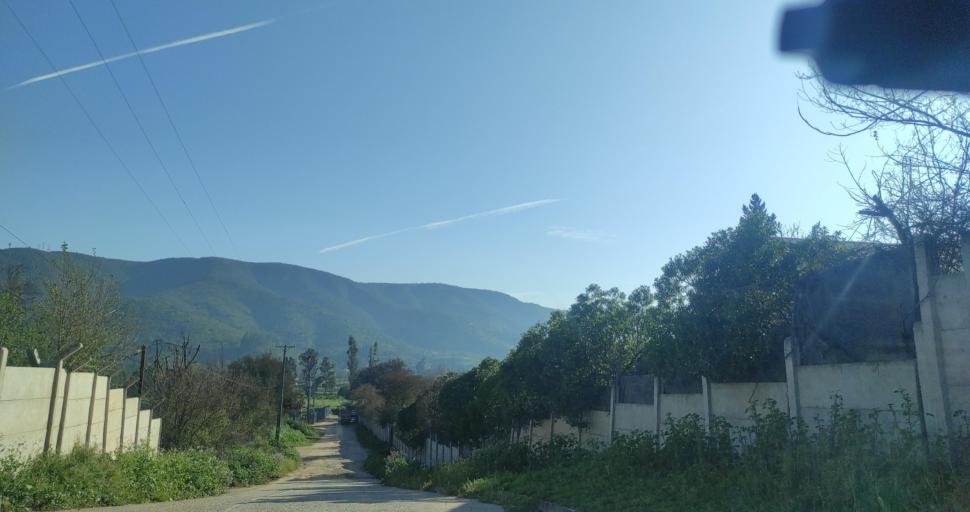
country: CL
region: Valparaiso
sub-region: Provincia de Marga Marga
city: Limache
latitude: -33.0023
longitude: -71.2535
